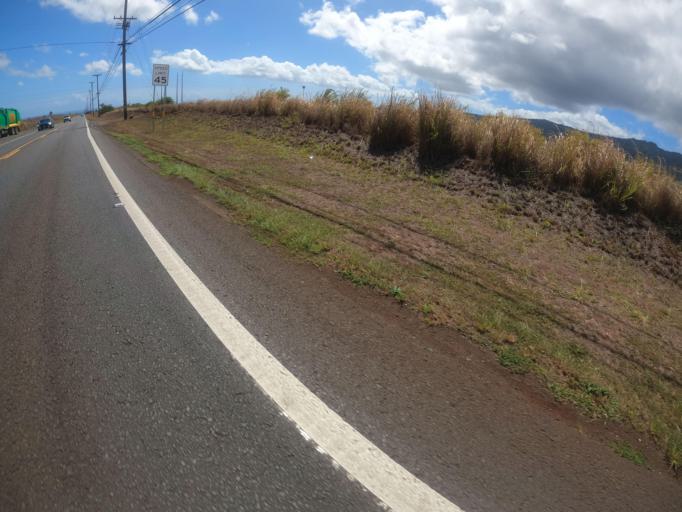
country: US
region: Hawaii
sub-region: Honolulu County
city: Village Park
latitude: 21.4166
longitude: -158.0473
